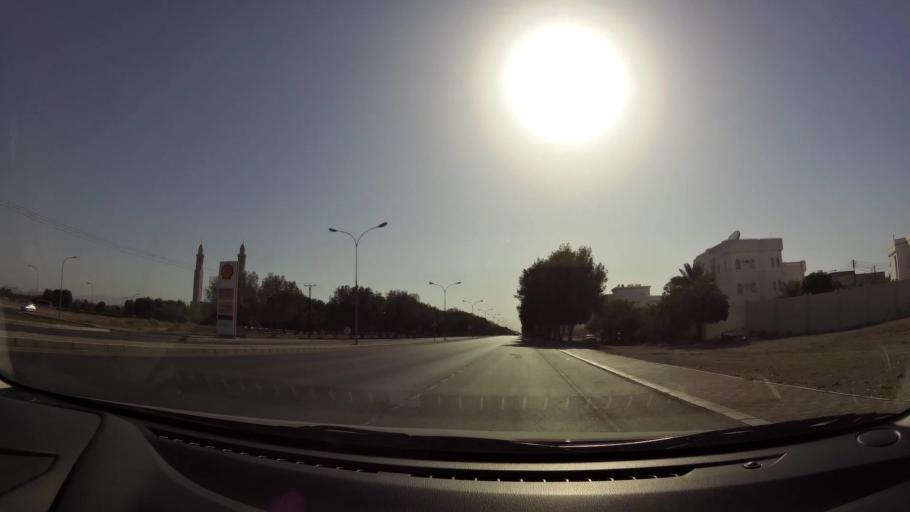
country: OM
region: Muhafazat Masqat
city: As Sib al Jadidah
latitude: 23.6151
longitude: 58.2134
